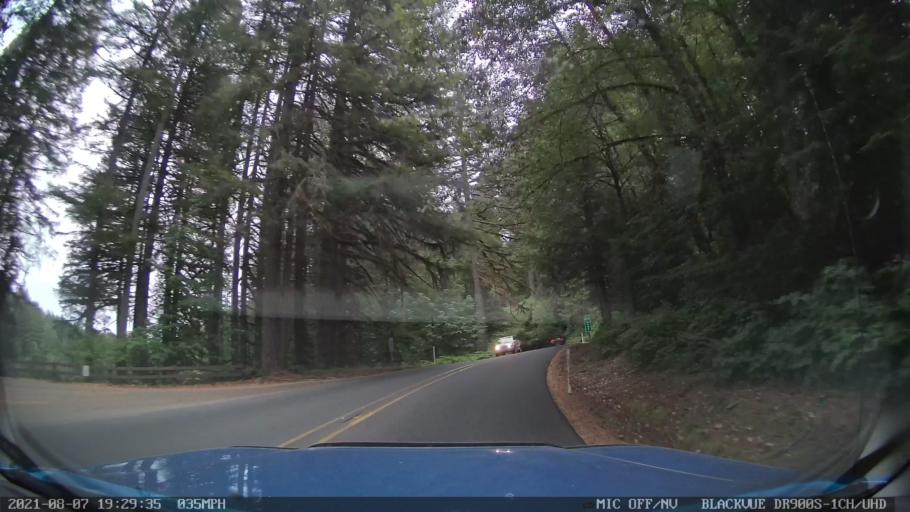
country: US
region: Oregon
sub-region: Linn County
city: Lyons
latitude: 44.8837
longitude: -122.6272
